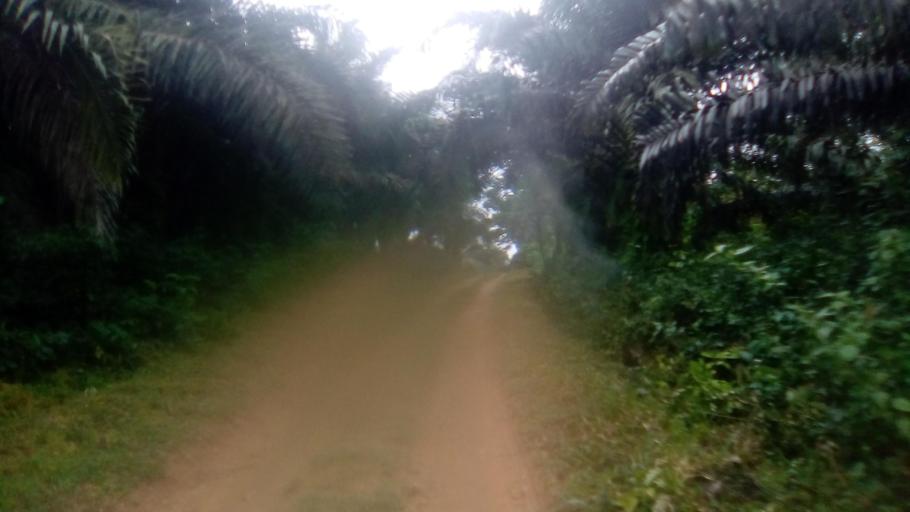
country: SL
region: Eastern Province
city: Kailahun
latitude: 8.2913
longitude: -10.5964
